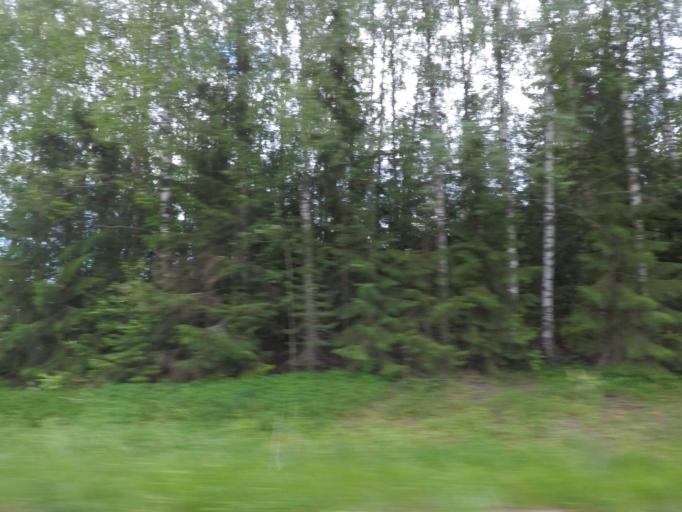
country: FI
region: Uusimaa
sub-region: Helsinki
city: Maentsaelae
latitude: 60.7509
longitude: 25.4319
